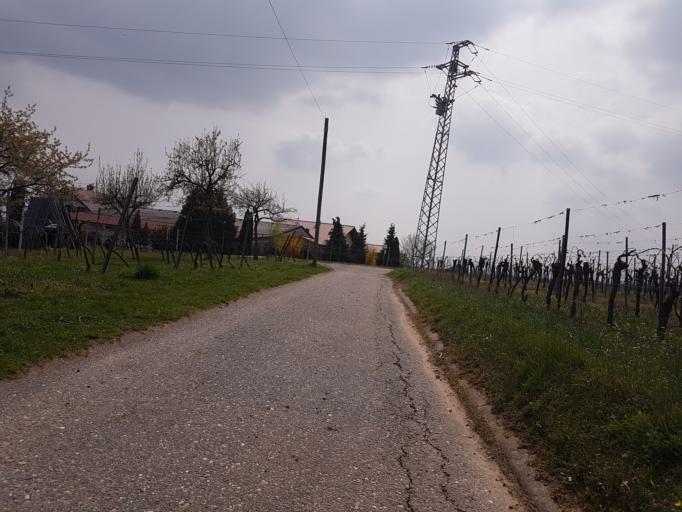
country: DE
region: Rheinland-Pfalz
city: Gleisweiler
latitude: 49.2453
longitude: 8.0725
